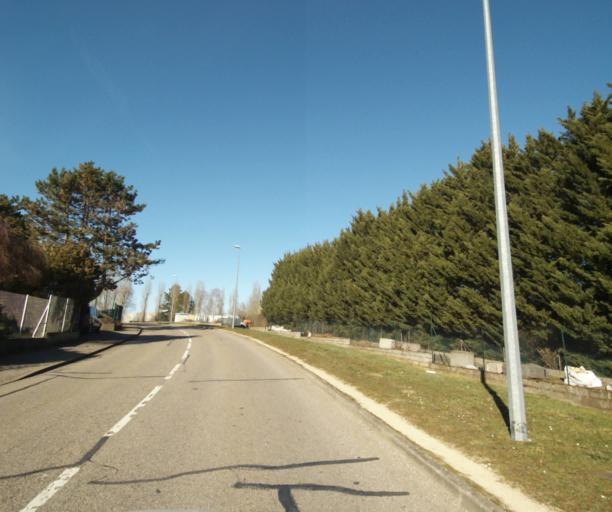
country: FR
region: Lorraine
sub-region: Departement de Meurthe-et-Moselle
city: Vandoeuvre-les-Nancy
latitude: 48.6458
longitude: 6.1856
